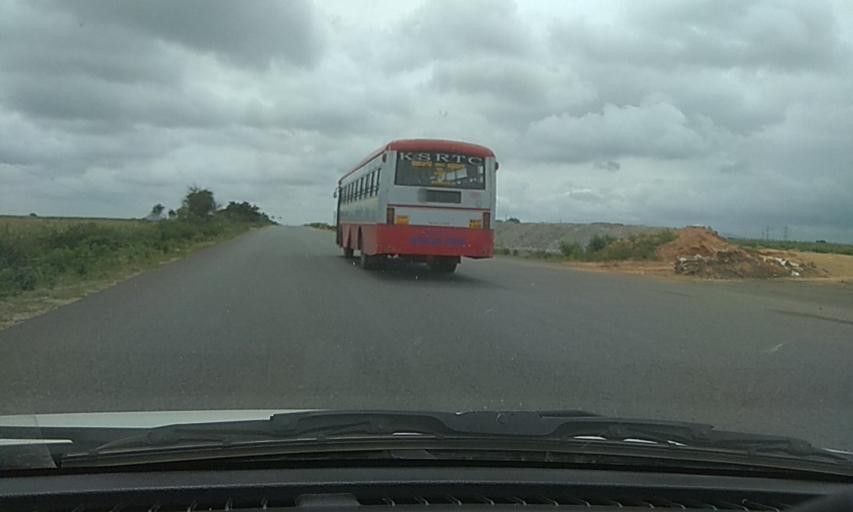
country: IN
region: Karnataka
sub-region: Chitradurga
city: Chitradurga
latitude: 14.2852
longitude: 76.2985
